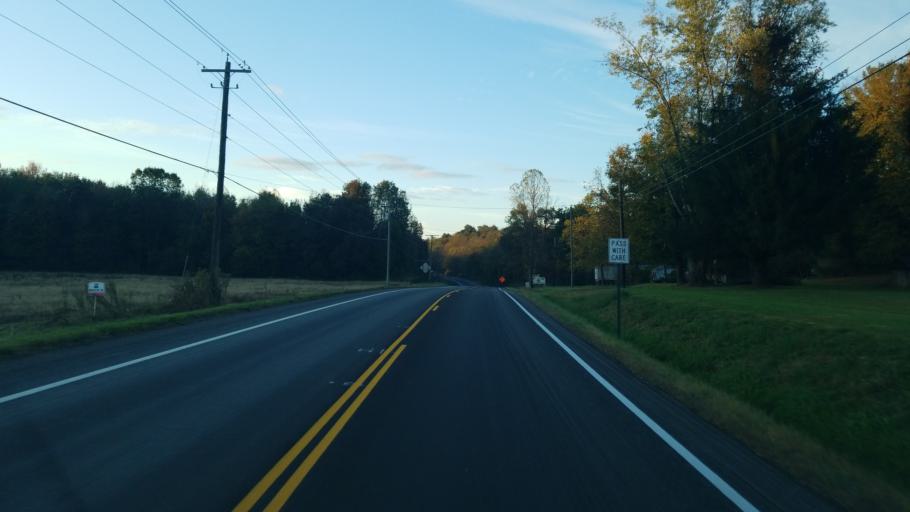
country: US
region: Ohio
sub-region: Vinton County
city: McArthur
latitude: 39.2238
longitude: -82.4809
